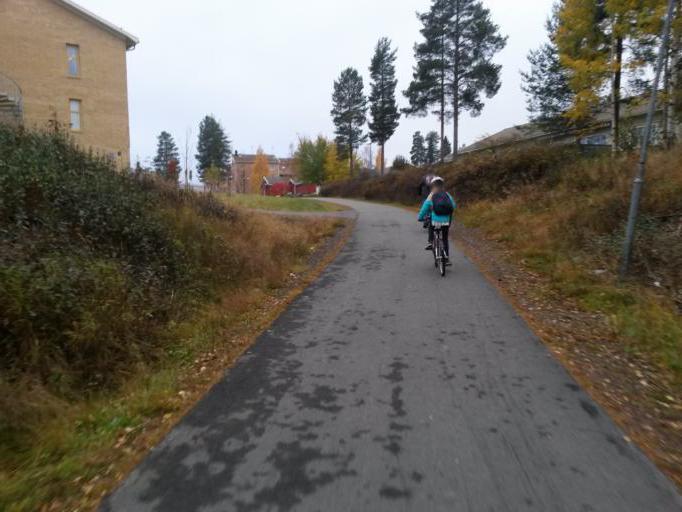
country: SE
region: Vaesterbotten
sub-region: Skelleftea Kommun
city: Soedra Bergsbyn
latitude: 64.7543
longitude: 21.0288
